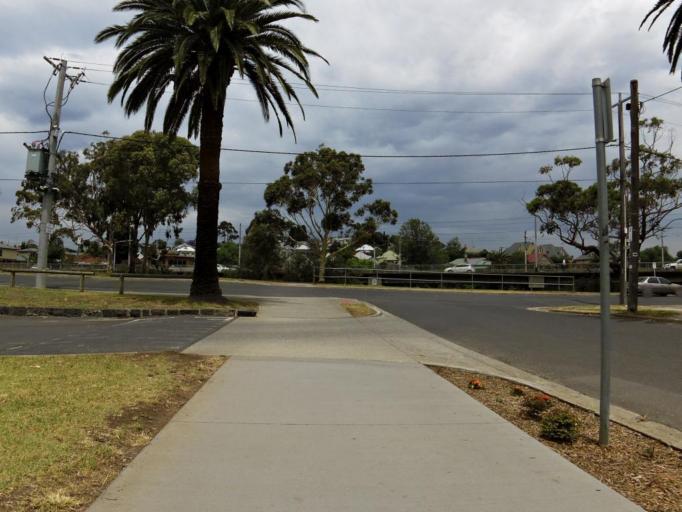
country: AU
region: Victoria
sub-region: Moonee Valley
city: Moonee Ponds
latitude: -37.7693
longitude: 144.9007
